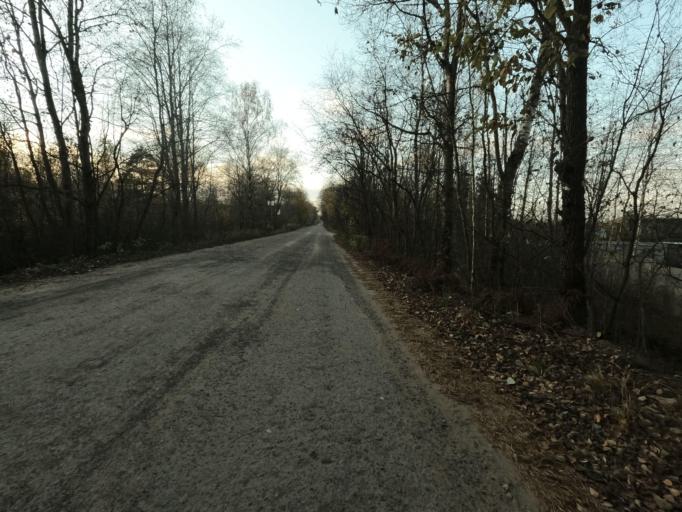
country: RU
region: Leningrad
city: Mga
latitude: 59.7631
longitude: 31.2528
